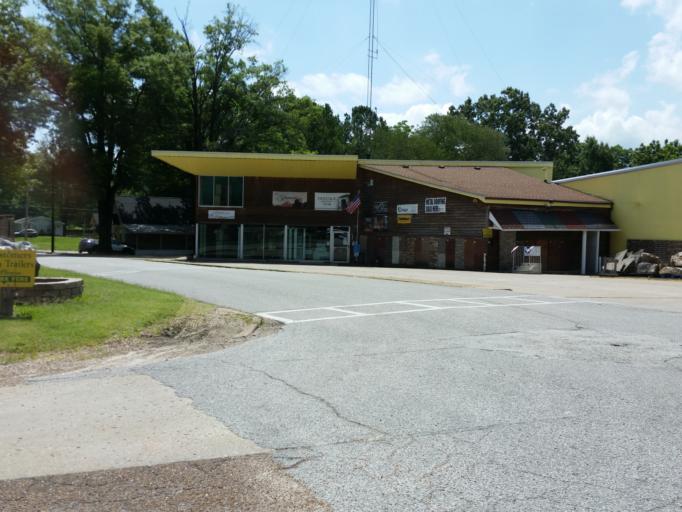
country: US
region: Tennessee
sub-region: Weakley County
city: Martin
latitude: 36.3403
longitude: -88.8496
